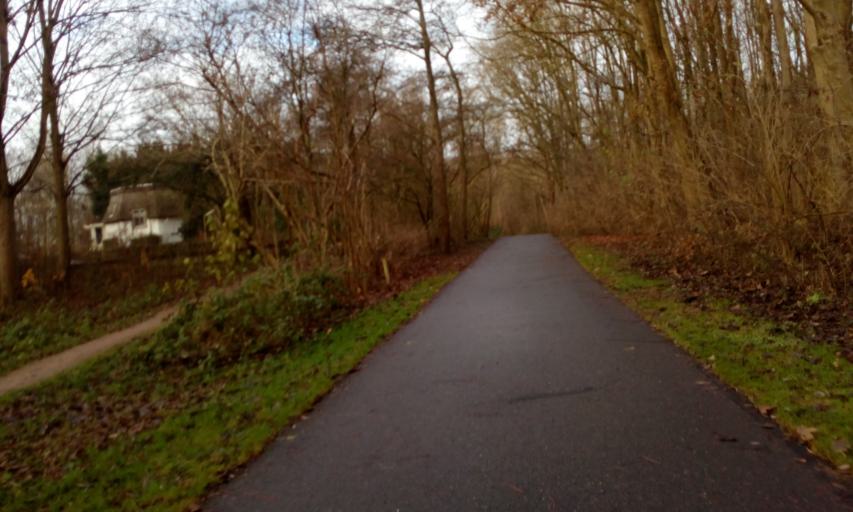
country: NL
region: South Holland
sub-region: Gemeente Lansingerland
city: Bergschenhoek
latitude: 51.9627
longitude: 4.5171
